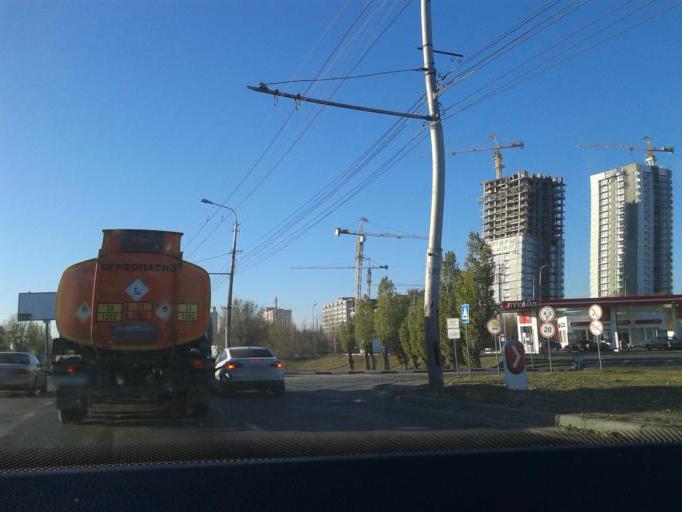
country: RU
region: Volgograd
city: Volgograd
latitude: 48.6279
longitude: 44.4270
